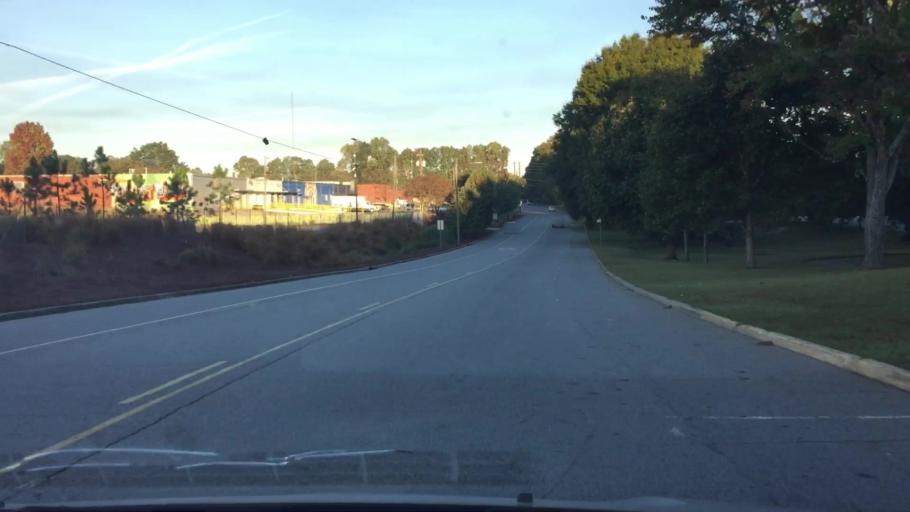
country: US
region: Georgia
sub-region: Fulton County
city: Atlanta
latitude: 33.7311
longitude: -84.4191
